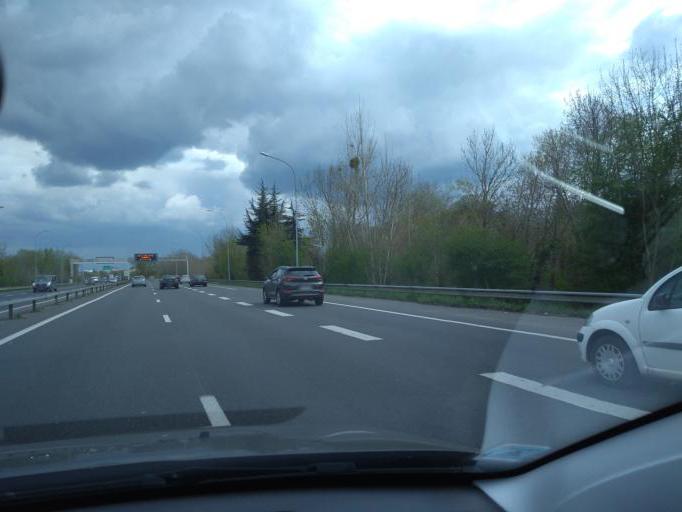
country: FR
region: Pays de la Loire
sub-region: Departement de Maine-et-Loire
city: Angers
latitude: 47.4647
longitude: -0.5755
